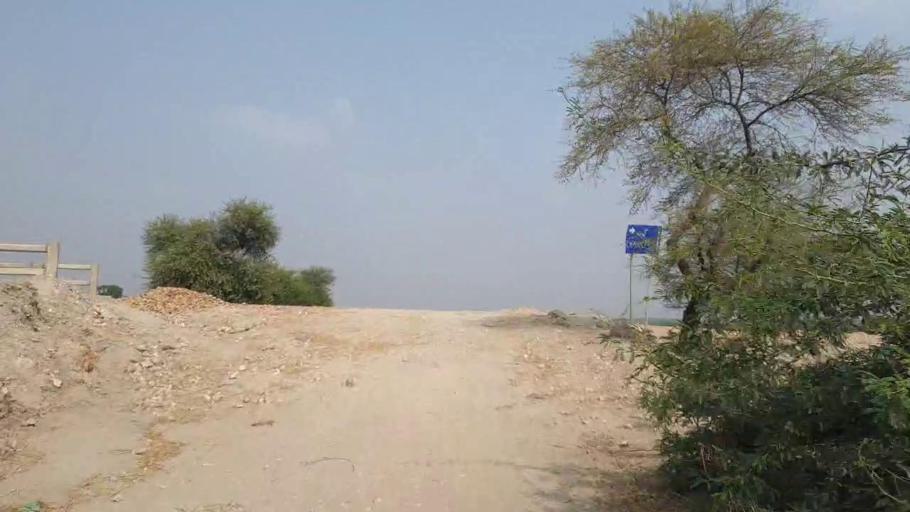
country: PK
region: Sindh
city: Kario
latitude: 24.7822
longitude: 68.5212
